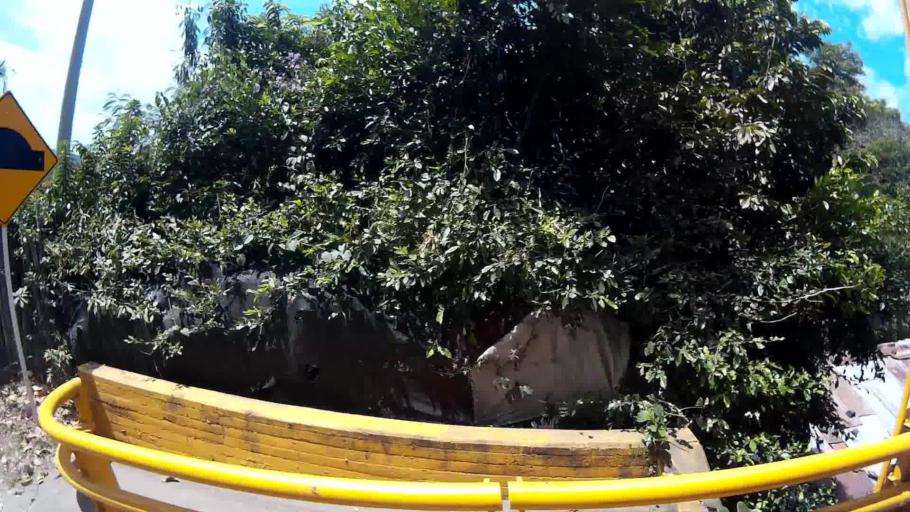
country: CO
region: Risaralda
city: La Virginia
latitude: 4.8851
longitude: -75.8697
